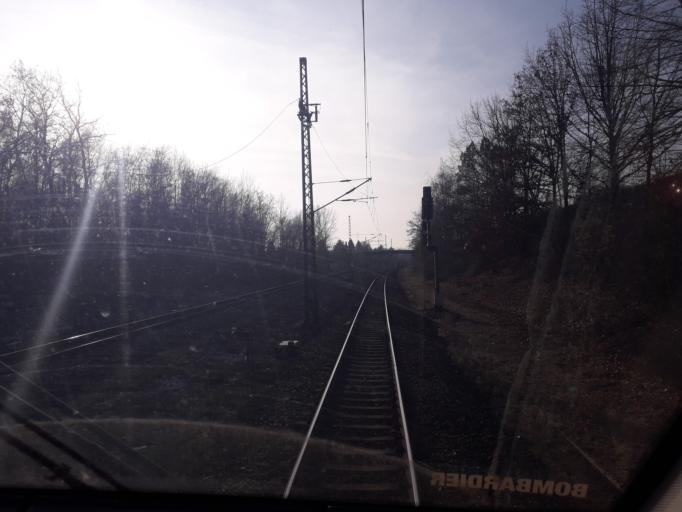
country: DE
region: Berlin
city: Altglienicke
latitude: 52.4113
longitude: 13.5505
